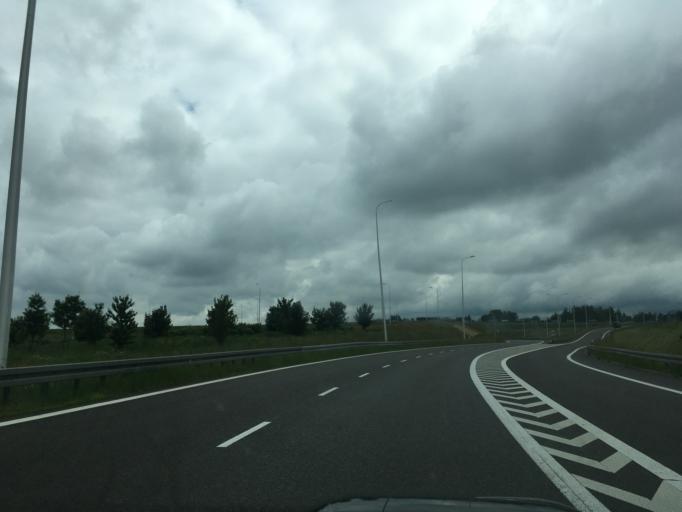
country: PL
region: Lublin Voivodeship
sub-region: Powiat lubelski
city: Jastkow
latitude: 51.2855
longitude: 22.4474
